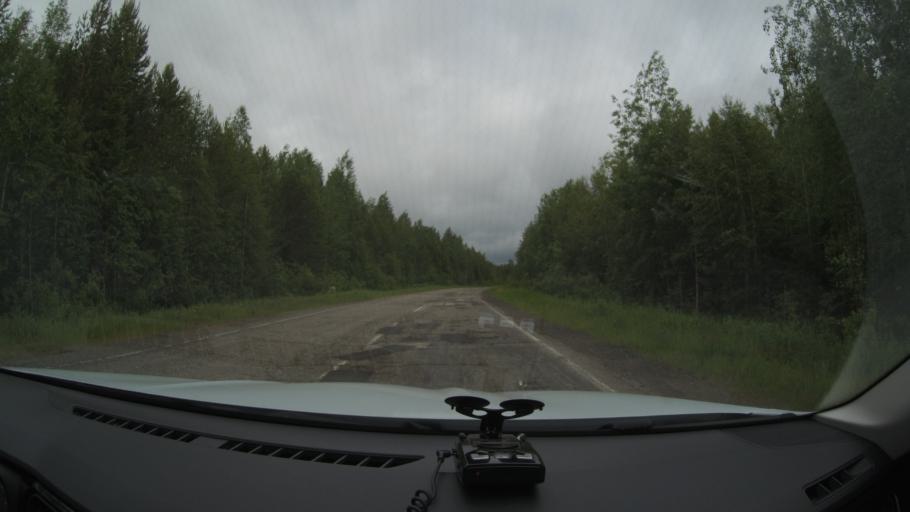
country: RU
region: Komi Republic
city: Nizhniy Odes
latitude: 63.6536
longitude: 54.6677
